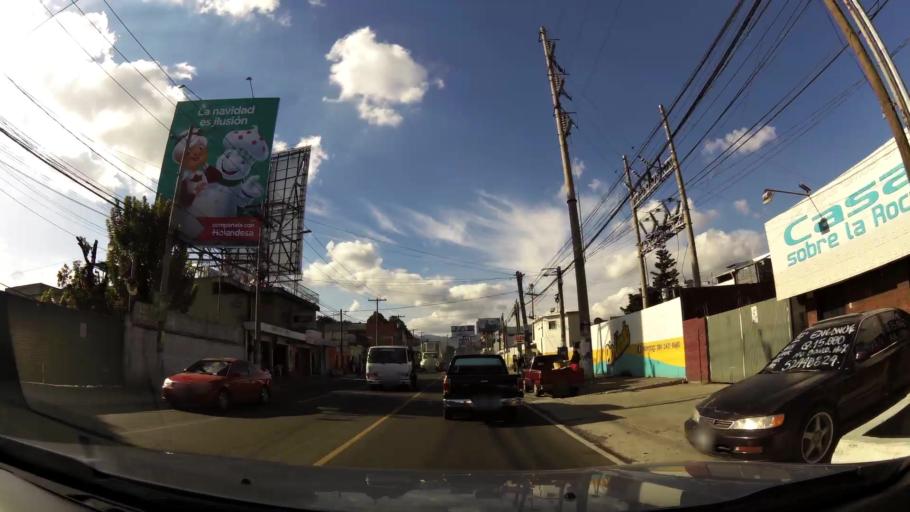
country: GT
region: Guatemala
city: Villa Nueva
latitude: 14.5163
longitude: -90.5778
